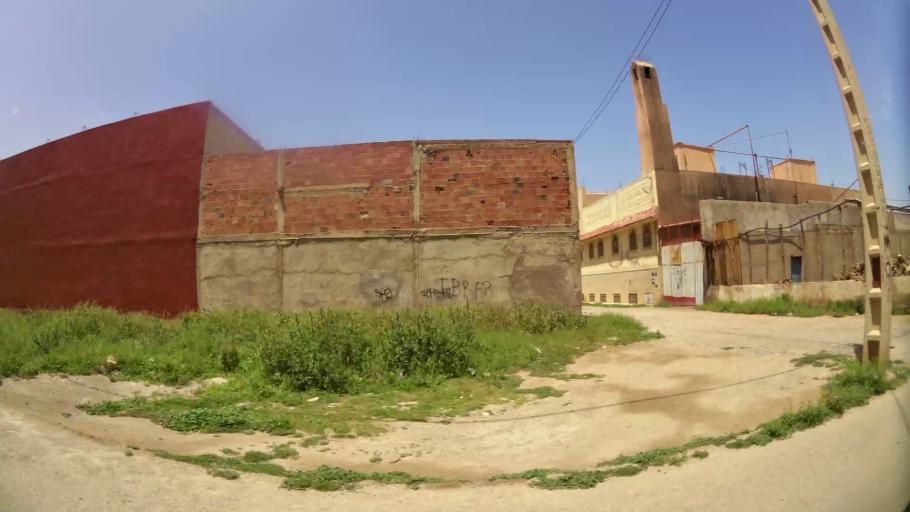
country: MA
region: Oriental
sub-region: Oujda-Angad
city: Oujda
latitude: 34.6983
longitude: -1.8939
